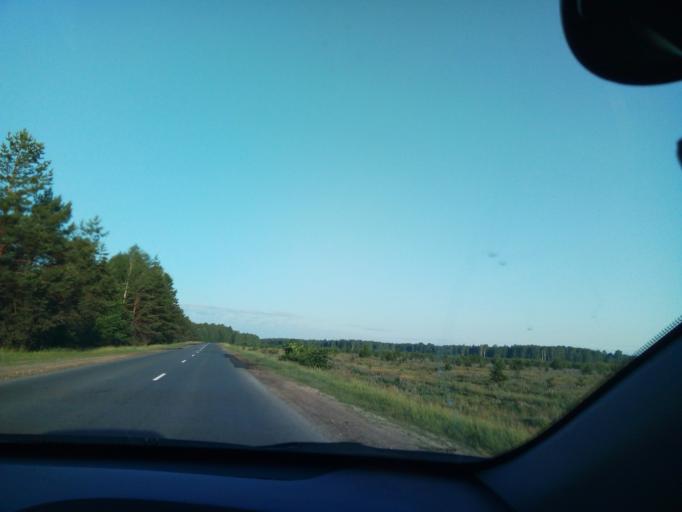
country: RU
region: Nizjnij Novgorod
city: Satis
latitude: 54.9311
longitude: 43.2105
